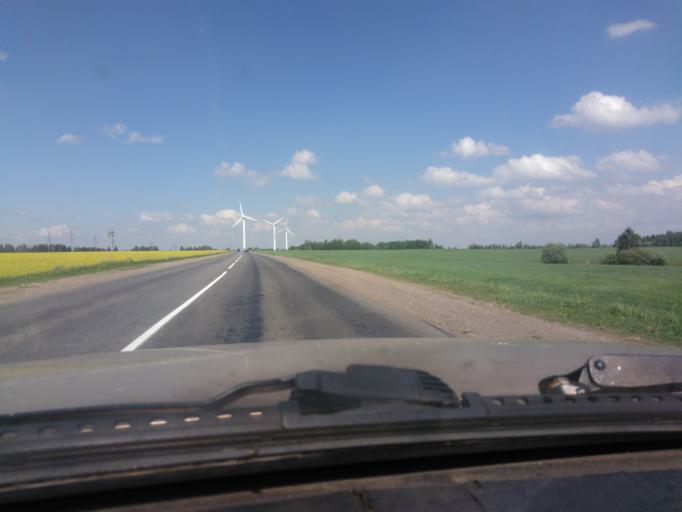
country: BY
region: Mogilev
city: Palykavichy Pyershyya
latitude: 53.9738
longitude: 30.3495
